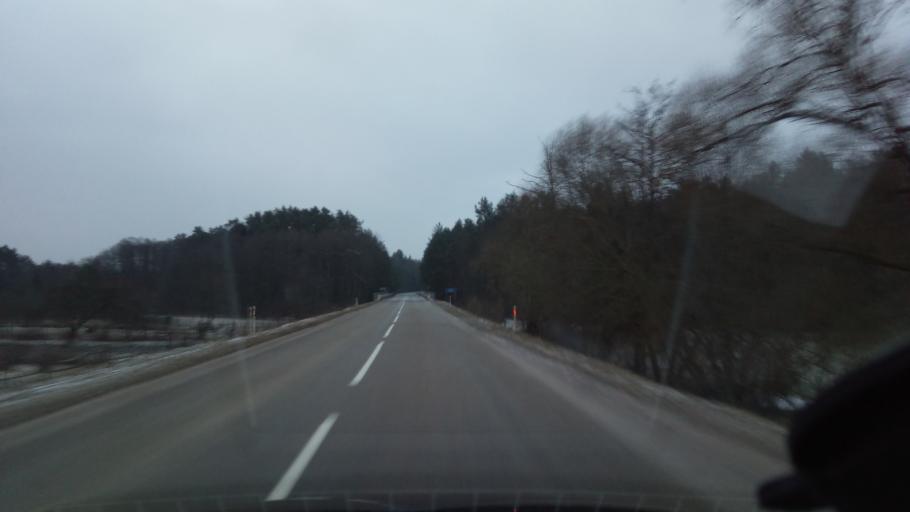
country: LT
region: Vilnius County
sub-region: Trakai
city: Rudiskes
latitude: 54.3438
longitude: 24.8447
